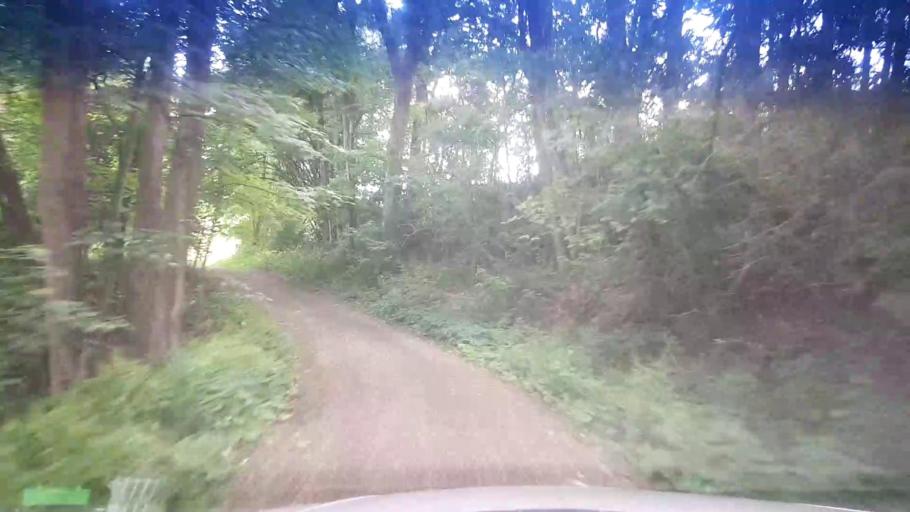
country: DE
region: Bavaria
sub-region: Upper Franconia
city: Memmelsdorf
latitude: 49.9530
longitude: 10.9870
